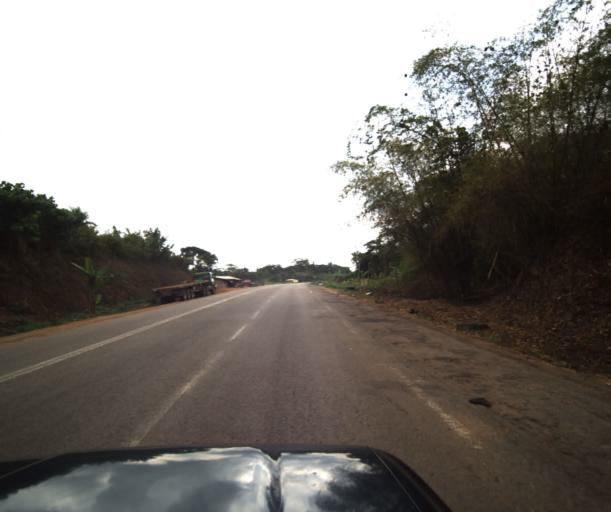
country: CM
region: Littoral
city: Edea
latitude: 3.8286
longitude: 10.3969
